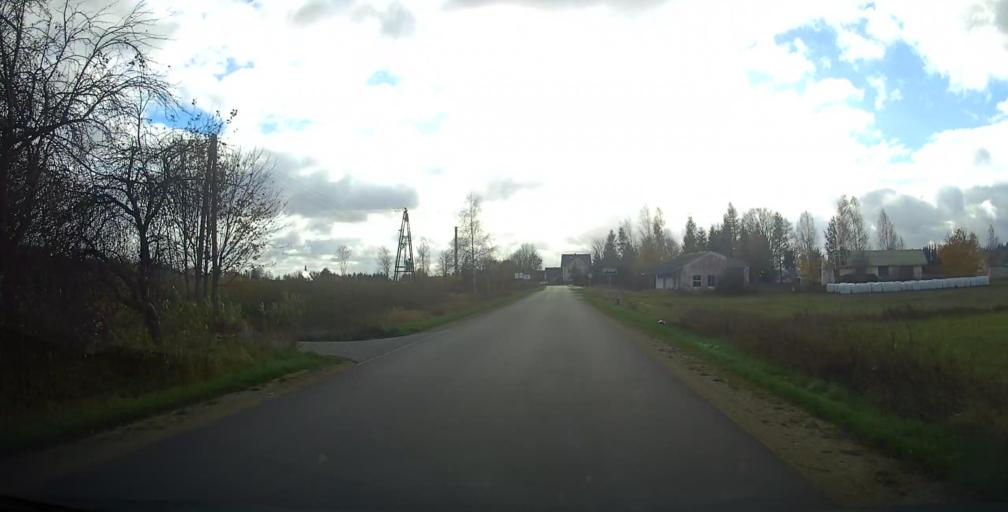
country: PL
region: Podlasie
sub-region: Suwalki
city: Suwalki
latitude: 54.2928
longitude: 22.8787
